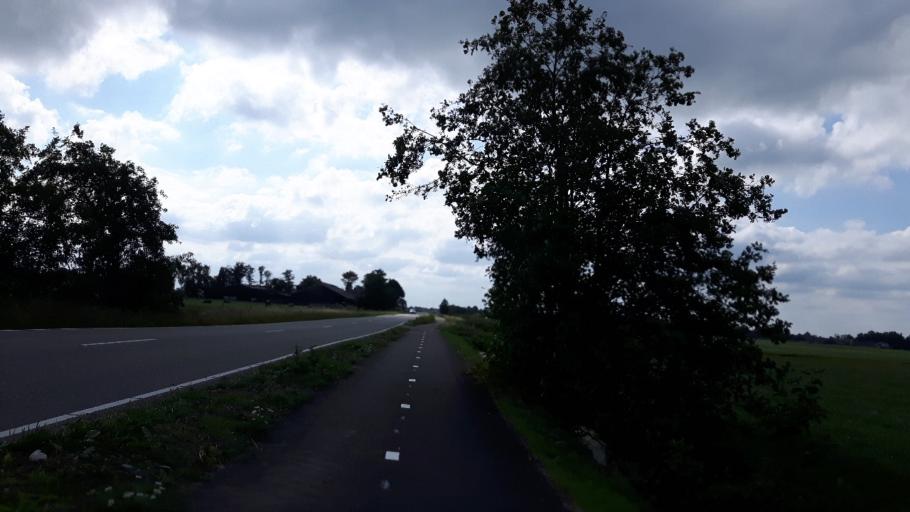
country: NL
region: Utrecht
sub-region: Gemeente Woerden
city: Woerden
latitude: 52.1316
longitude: 4.8584
